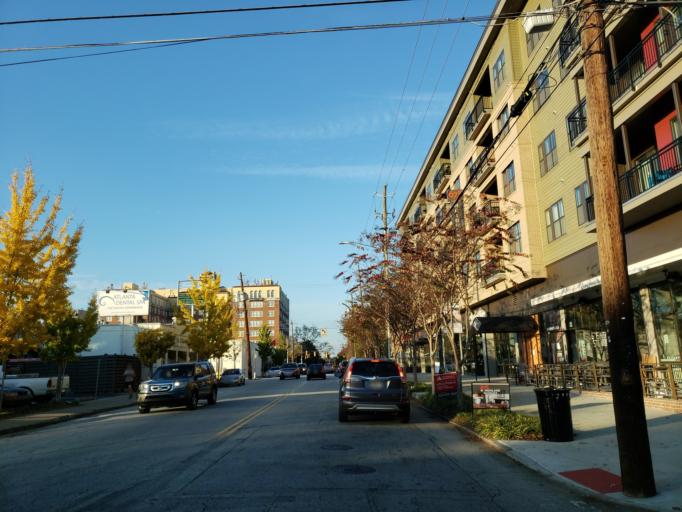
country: US
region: Georgia
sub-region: DeKalb County
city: Druid Hills
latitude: 33.7722
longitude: -84.3525
